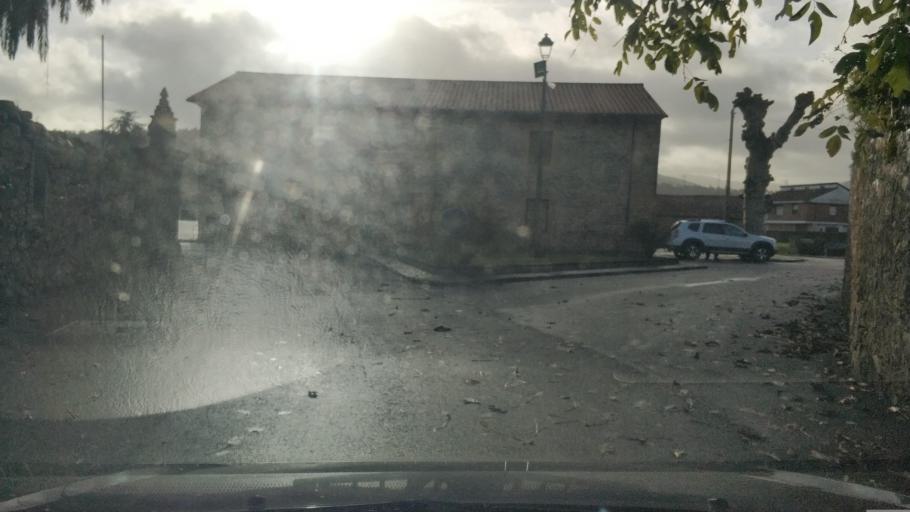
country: ES
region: Cantabria
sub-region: Provincia de Cantabria
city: Luzmela
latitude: 43.3362
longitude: -4.1792
